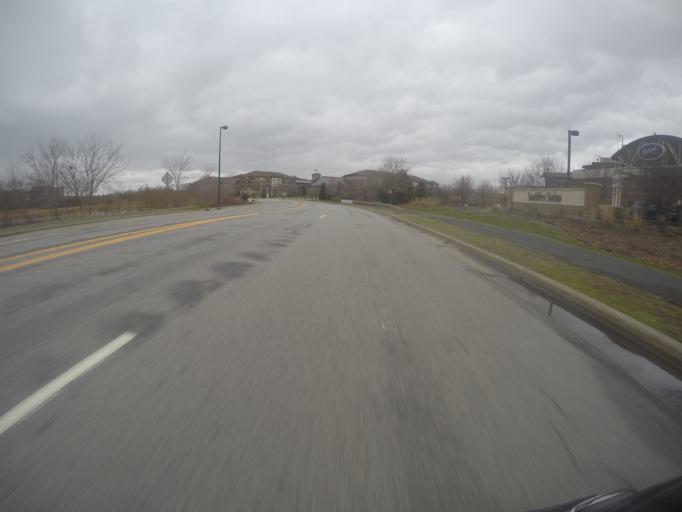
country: US
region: Minnesota
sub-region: Hennepin County
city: Eden Prairie
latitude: 44.8591
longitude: -93.4442
